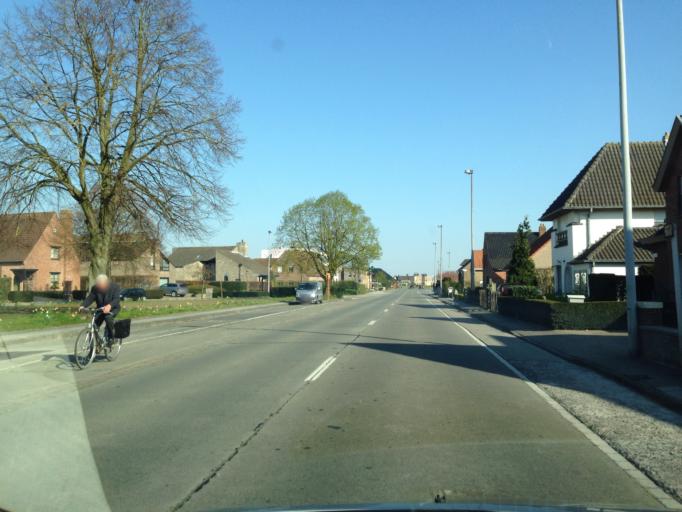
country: BE
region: Flanders
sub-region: Provincie West-Vlaanderen
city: Zedelgem
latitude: 51.1390
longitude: 3.1419
